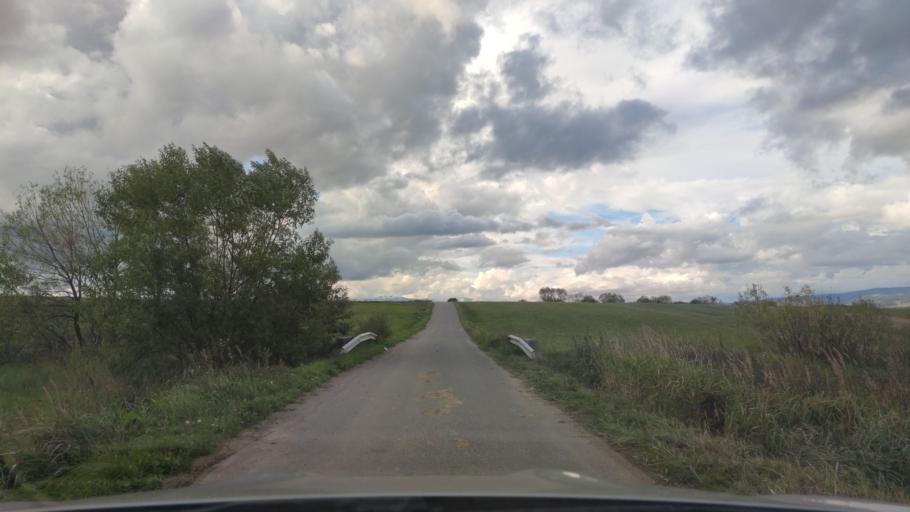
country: RO
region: Harghita
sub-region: Comuna Subcetate
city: Subcetate
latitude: 46.8195
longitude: 25.4324
